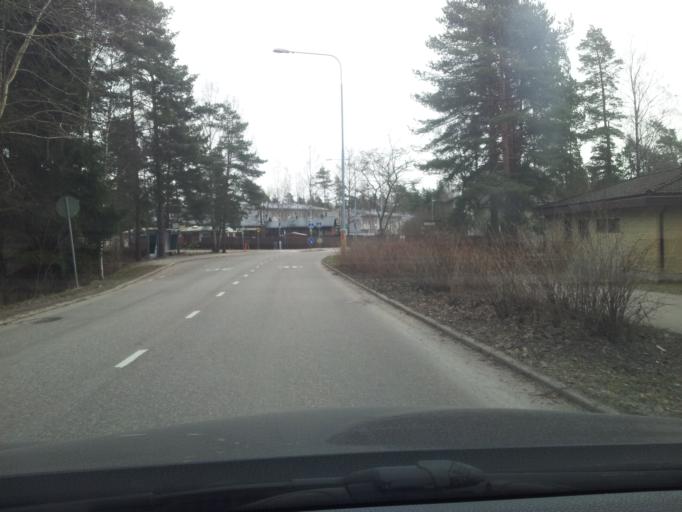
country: FI
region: Uusimaa
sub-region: Helsinki
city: Otaniemi
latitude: 60.2047
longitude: 24.8087
